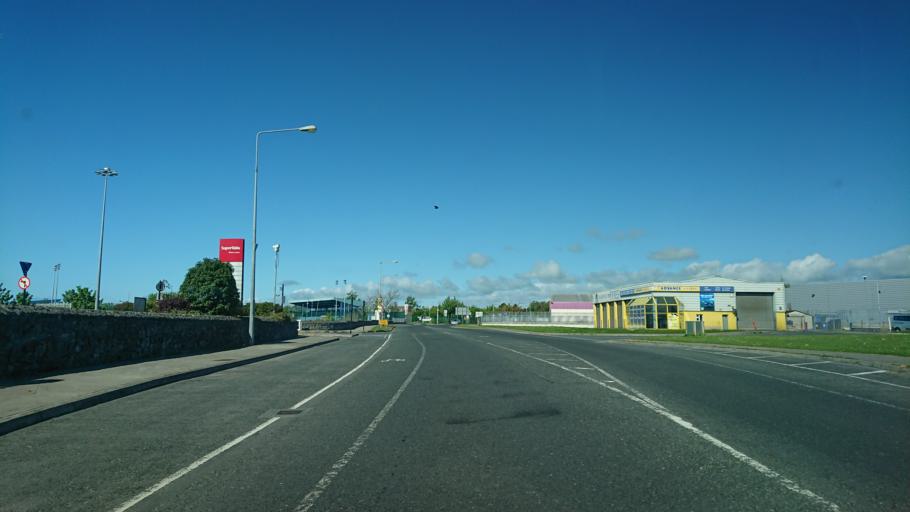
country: IE
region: Munster
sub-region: Waterford
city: Waterford
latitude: 52.2472
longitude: -7.1212
